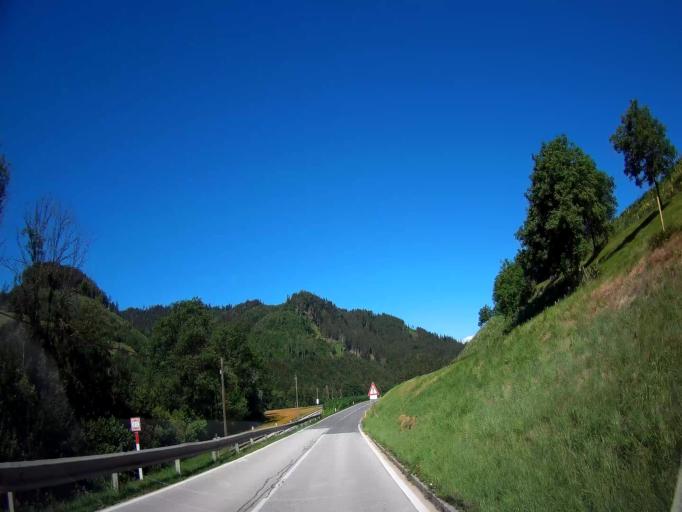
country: AT
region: Carinthia
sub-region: Politischer Bezirk Sankt Veit an der Glan
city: Bruckl
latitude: 46.7541
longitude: 14.5029
